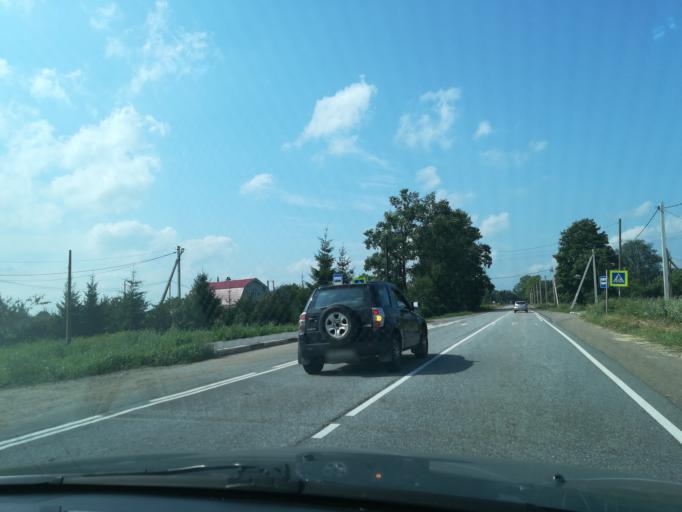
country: RU
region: Leningrad
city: Kopor'ye
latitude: 59.7051
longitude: 29.0629
